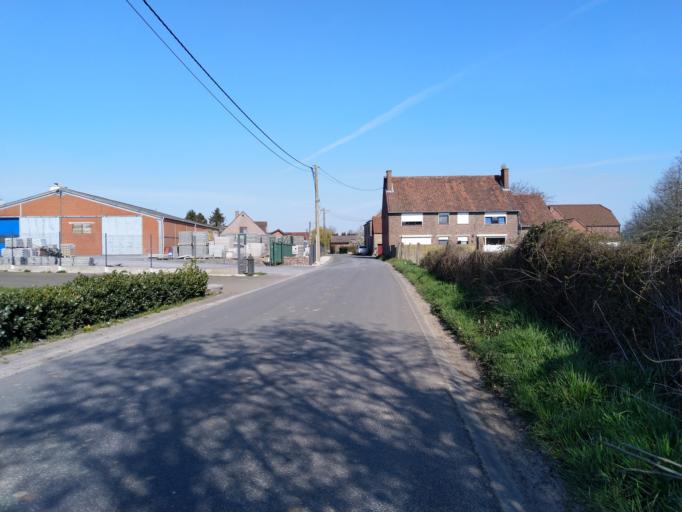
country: BE
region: Wallonia
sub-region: Province du Hainaut
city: Lens
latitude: 50.5517
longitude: 3.8844
